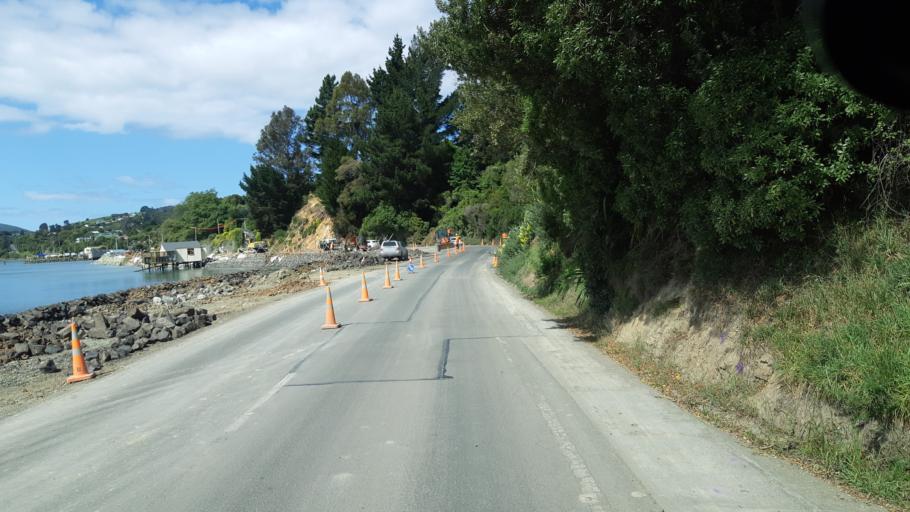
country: NZ
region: Otago
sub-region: Dunedin City
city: Portobello
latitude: -45.8490
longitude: 170.6140
